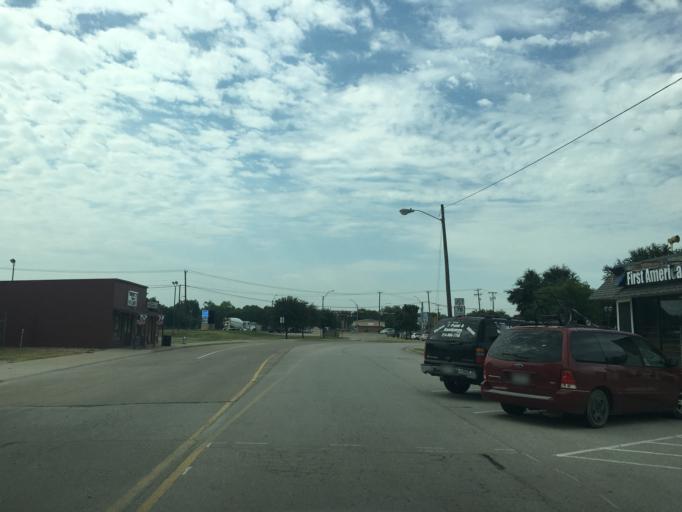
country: US
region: Texas
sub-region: Collin County
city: Wylie
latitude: 33.0139
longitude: -96.5390
